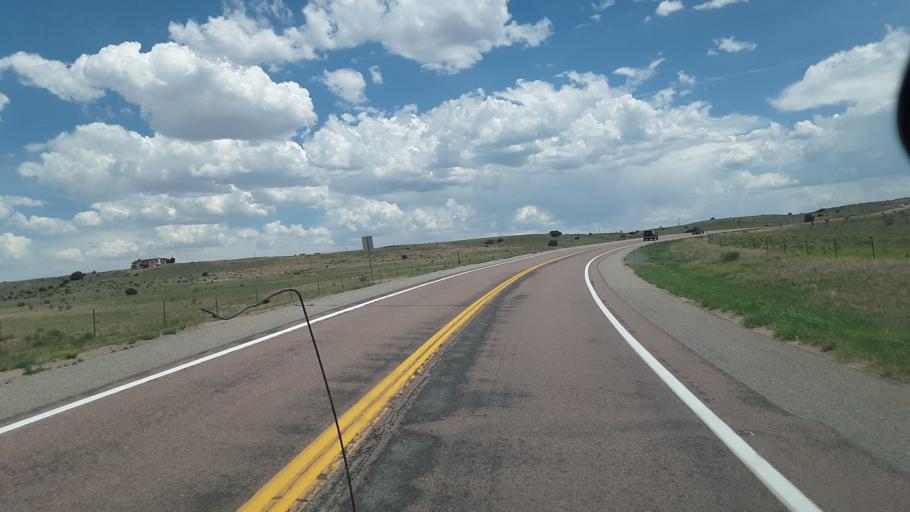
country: US
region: Colorado
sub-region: Fremont County
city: Florence
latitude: 38.2992
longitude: -105.0893
